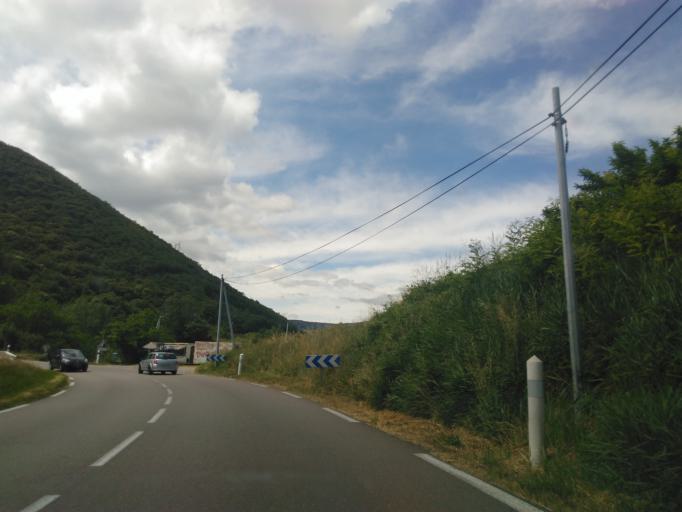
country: FR
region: Rhone-Alpes
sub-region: Departement de l'Ardeche
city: Le Teil
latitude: 44.5536
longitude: 4.6586
